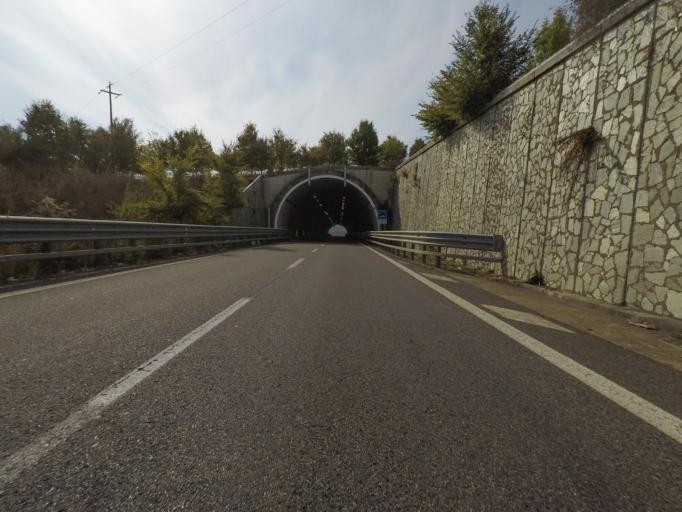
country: IT
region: Tuscany
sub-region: Provincia di Siena
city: Isola D'Arbia
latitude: 43.2715
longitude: 11.3317
